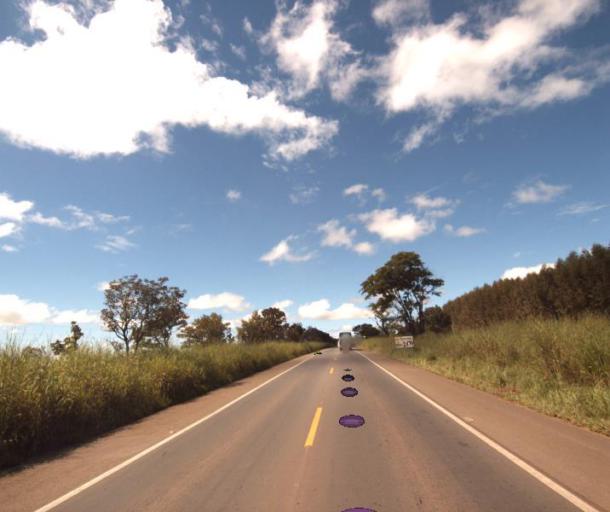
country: BR
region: Goias
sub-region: Rialma
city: Rialma
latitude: -15.4608
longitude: -49.5010
